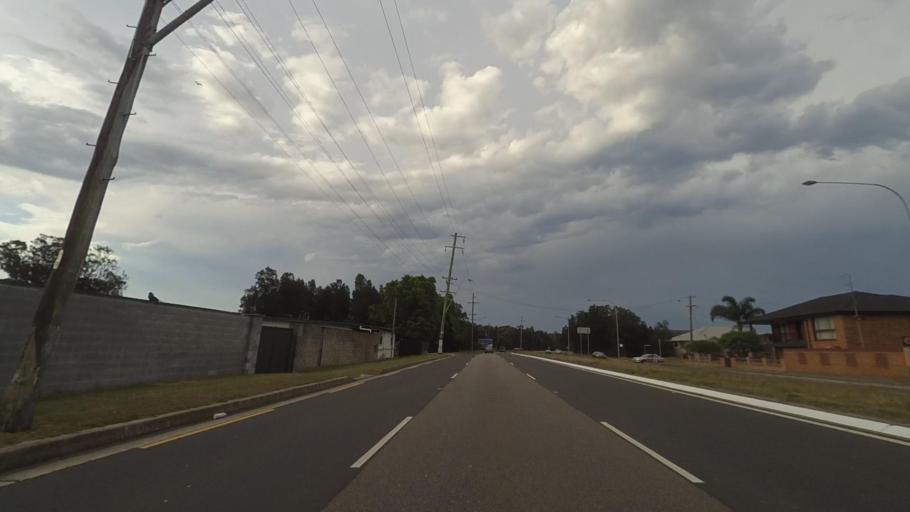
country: AU
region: New South Wales
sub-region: Shellharbour
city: Lake Illawarra
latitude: -34.5250
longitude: 150.8697
